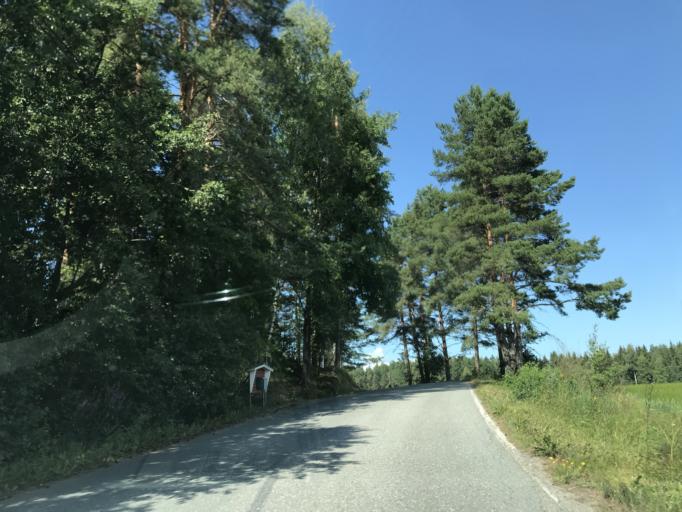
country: FI
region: Paijanne Tavastia
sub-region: Lahti
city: Asikkala
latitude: 61.1952
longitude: 25.6260
